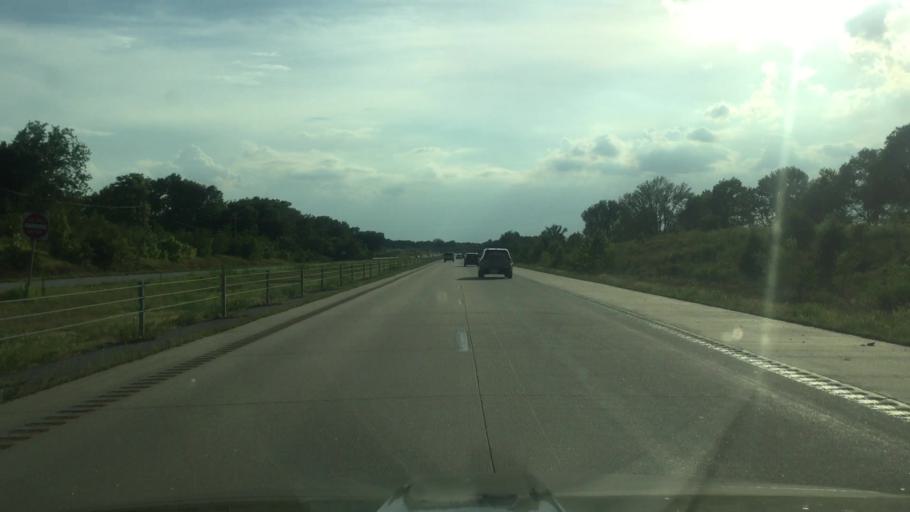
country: US
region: Missouri
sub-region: Jackson County
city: Lone Jack
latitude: 38.8701
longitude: -94.1609
